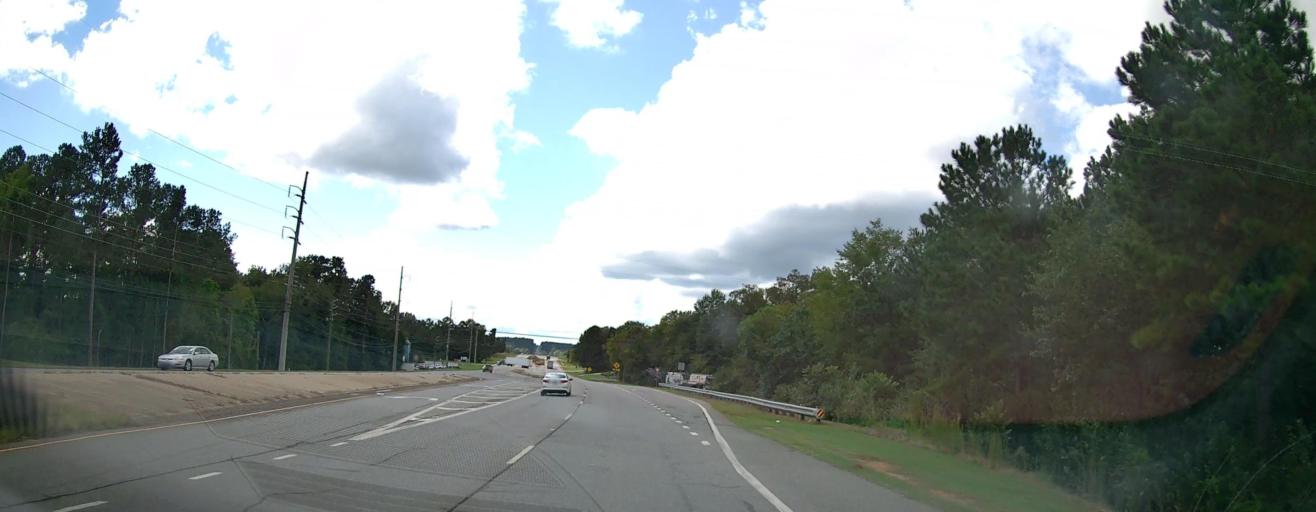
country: US
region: Georgia
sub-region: Baldwin County
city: Milledgeville
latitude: 33.0930
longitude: -83.2770
